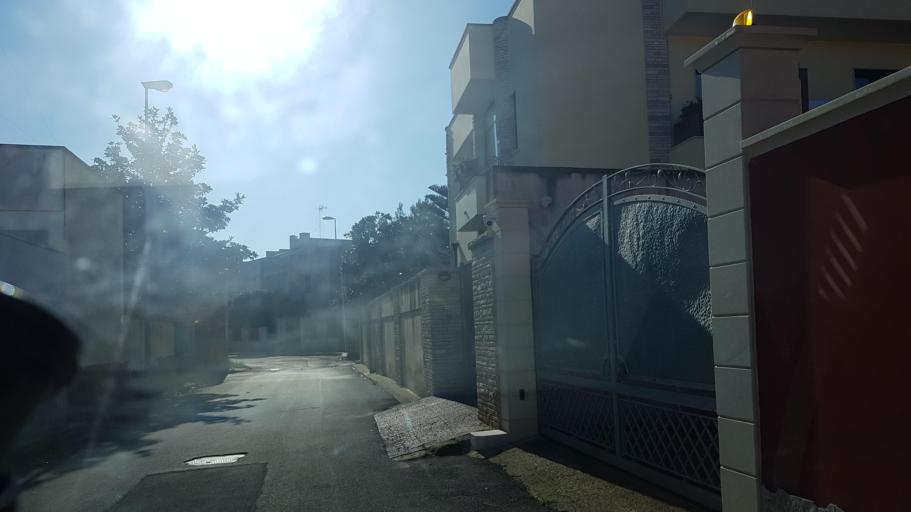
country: IT
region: Apulia
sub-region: Provincia di Lecce
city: Squinzano
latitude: 40.4332
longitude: 18.0448
